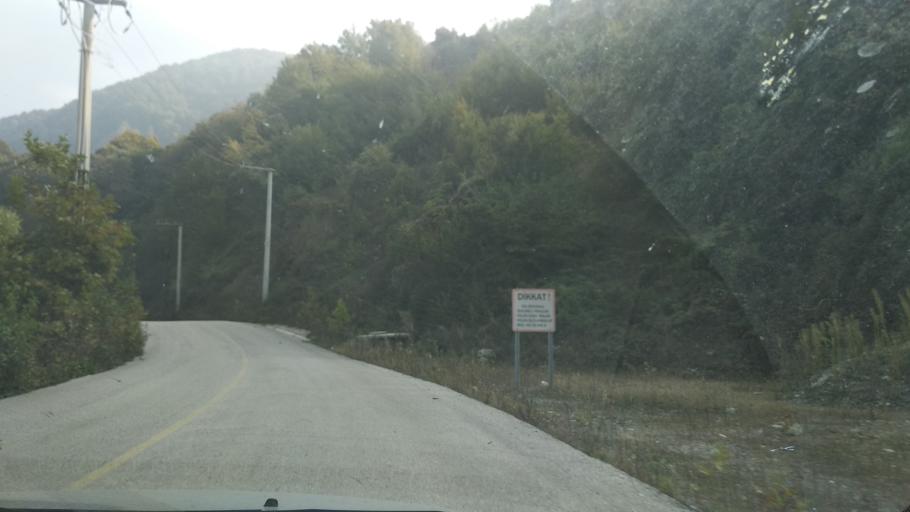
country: TR
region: Duzce
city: Duzce
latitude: 40.7357
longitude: 31.2097
